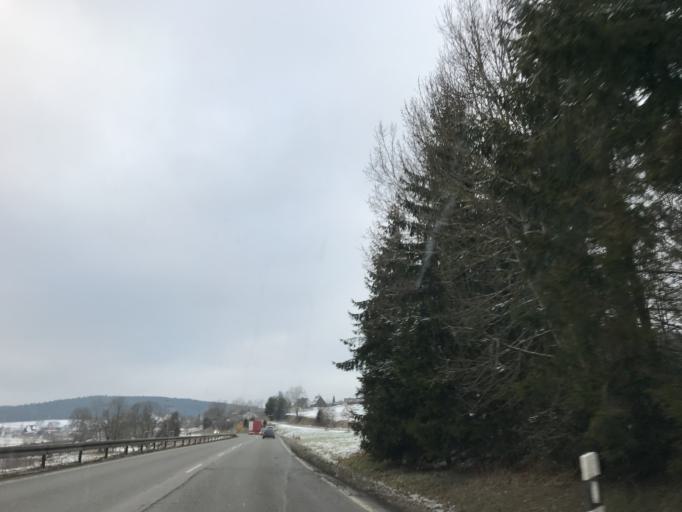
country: DE
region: Baden-Wuerttemberg
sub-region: Freiburg Region
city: Konigsfeld im Schwarzwald
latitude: 48.1269
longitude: 8.3828
